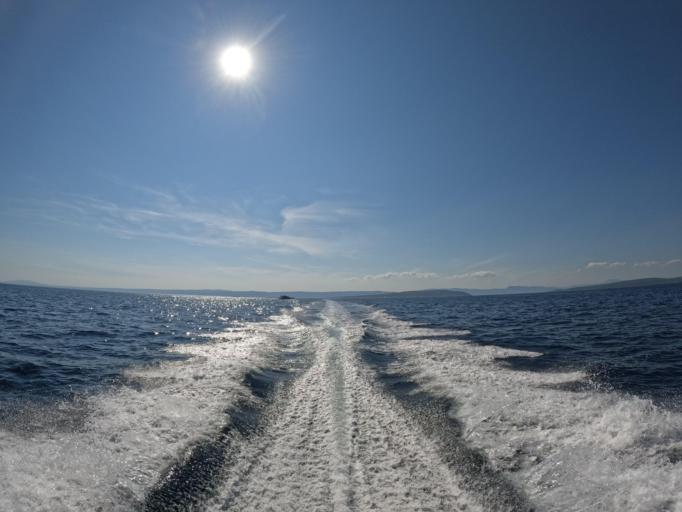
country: HR
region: Primorsko-Goranska
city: Punat
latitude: 44.9572
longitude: 14.6204
